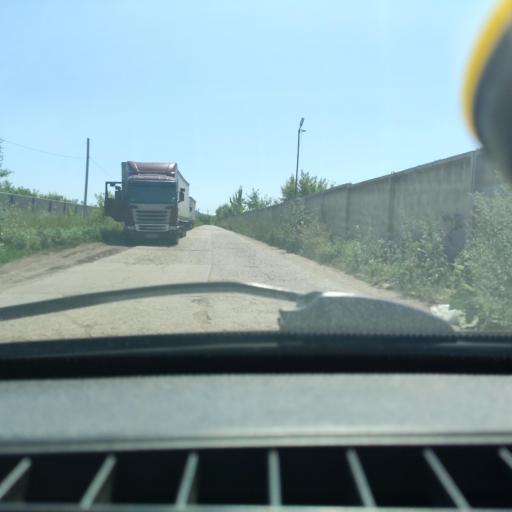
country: RU
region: Samara
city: Tol'yatti
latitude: 53.5711
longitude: 49.3611
